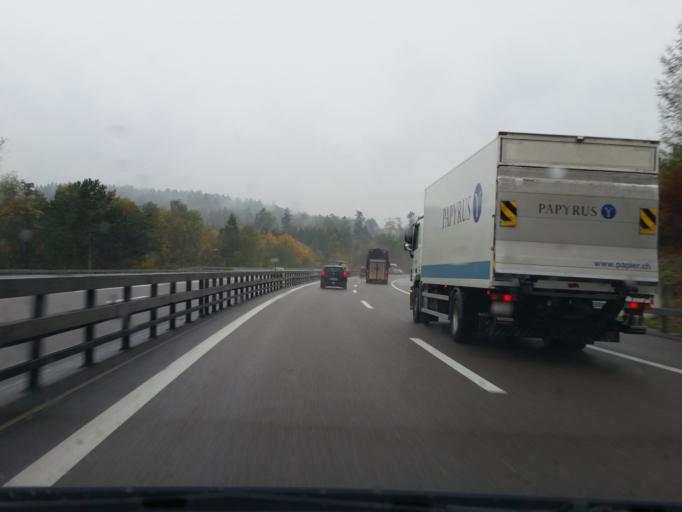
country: CH
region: Zurich
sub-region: Bezirk Winterthur
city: Veltheim
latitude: 47.5231
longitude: 8.7180
